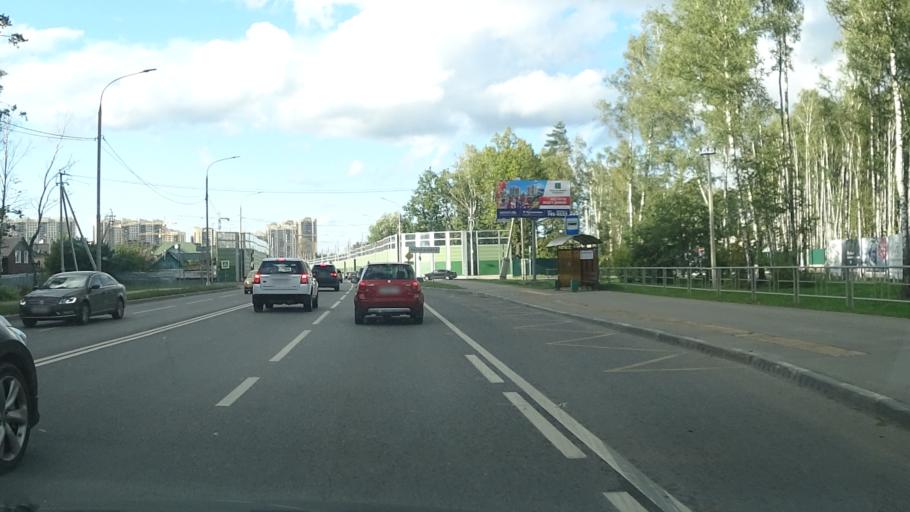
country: RU
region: Moscow
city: Novo-Peredelkino
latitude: 55.6264
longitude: 37.3376
